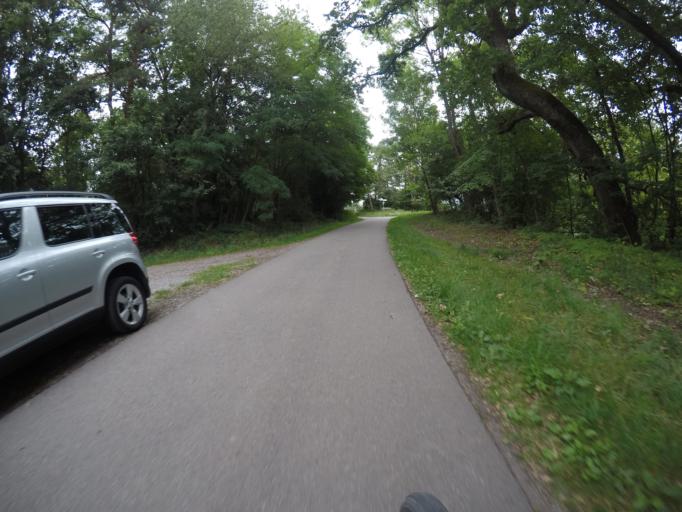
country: DE
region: Baden-Wuerttemberg
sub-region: Regierungsbezirk Stuttgart
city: Nufringen
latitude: 48.6047
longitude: 8.8852
